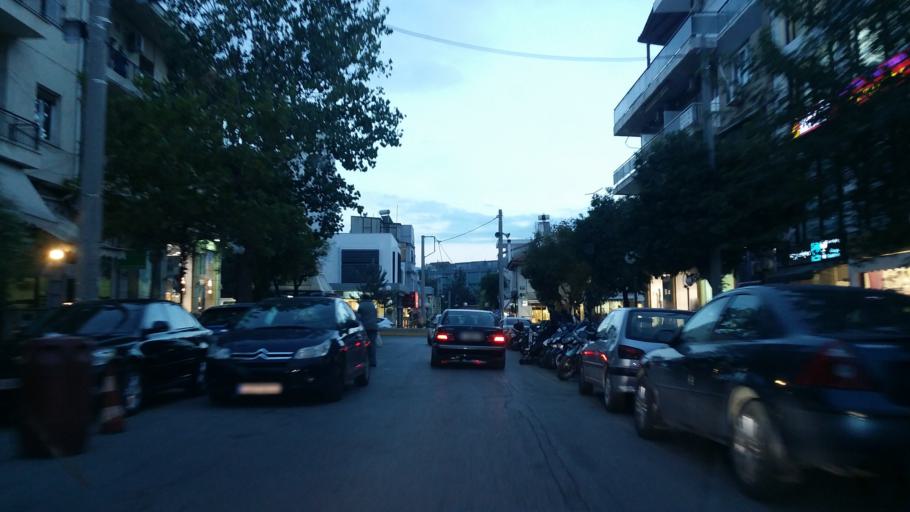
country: GR
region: Attica
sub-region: Nomarchia Athinas
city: Nea Ionia
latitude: 38.0421
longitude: 23.7516
